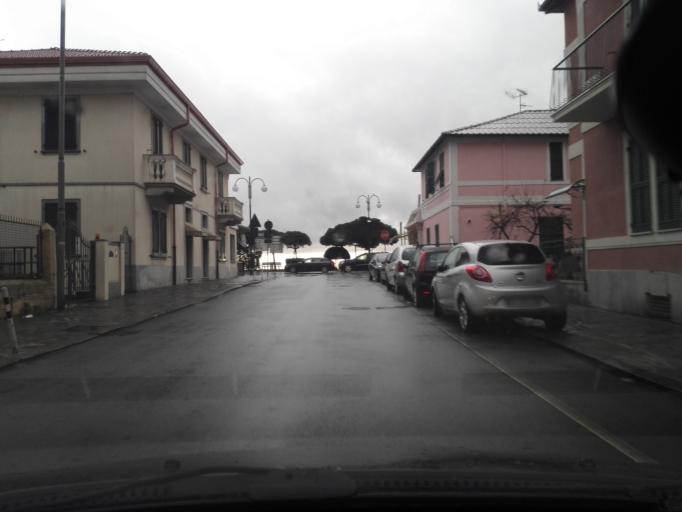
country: IT
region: Liguria
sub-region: Provincia di Genova
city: Chiavari
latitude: 44.3170
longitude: 9.3173
